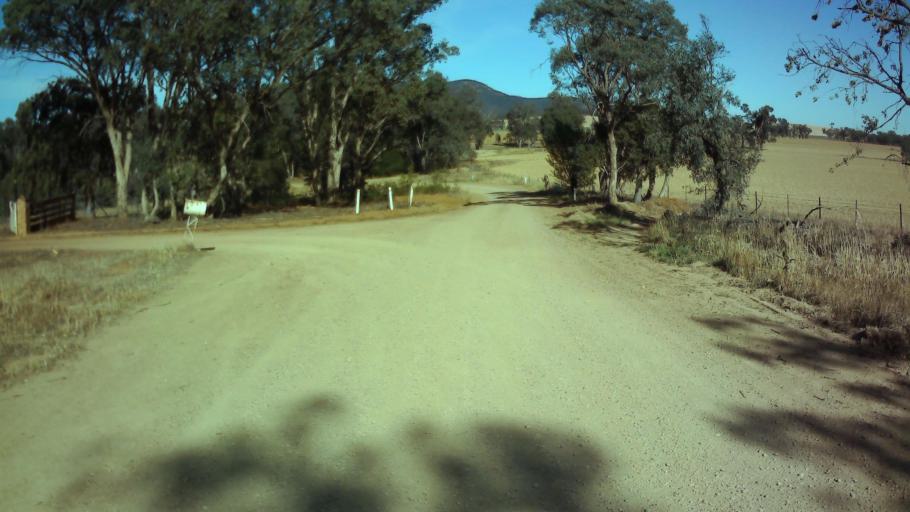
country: AU
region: New South Wales
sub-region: Weddin
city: Grenfell
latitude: -33.9030
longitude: 148.0425
